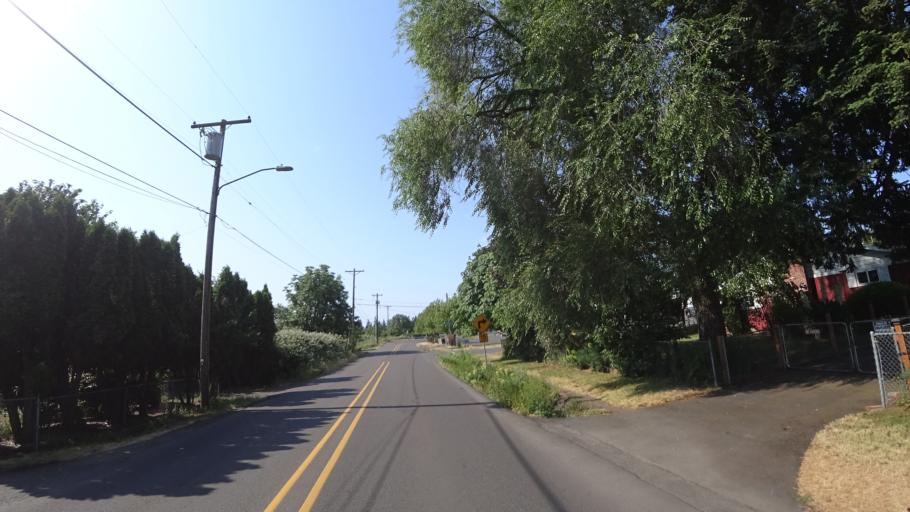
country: US
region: Oregon
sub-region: Multnomah County
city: Lents
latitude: 45.4597
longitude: -122.5894
